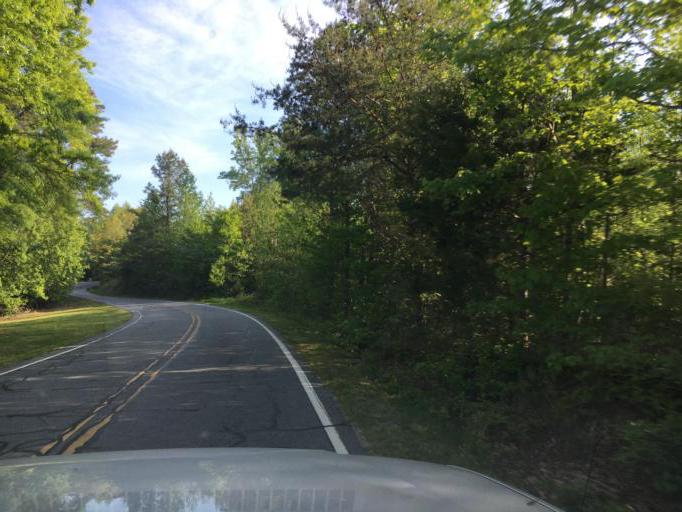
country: US
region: North Carolina
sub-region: Rutherford County
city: Rutherfordton
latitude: 35.3295
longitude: -81.9890
